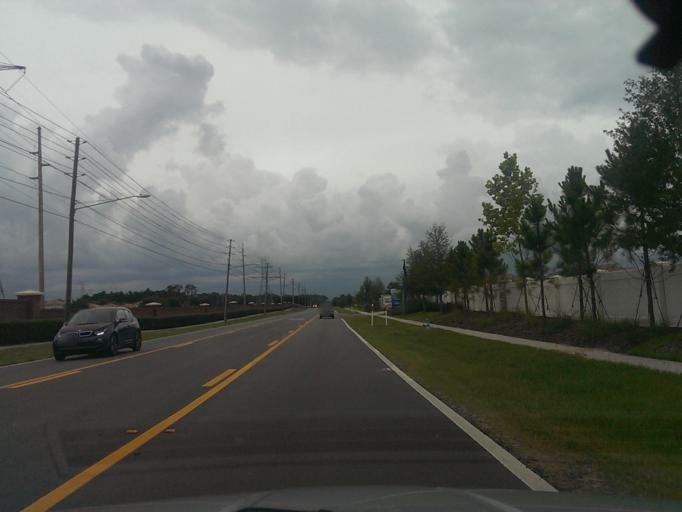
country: US
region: Florida
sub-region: Orange County
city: Windermere
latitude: 28.4643
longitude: -81.5566
